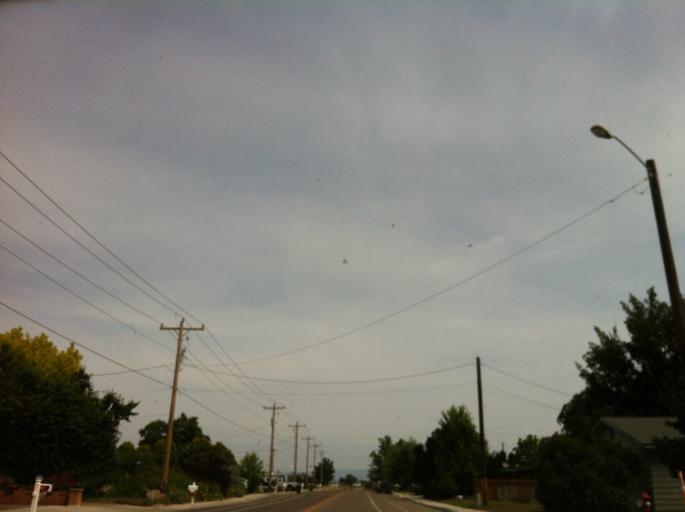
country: US
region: Idaho
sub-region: Payette County
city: Fruitland
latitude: 44.0254
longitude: -116.9320
